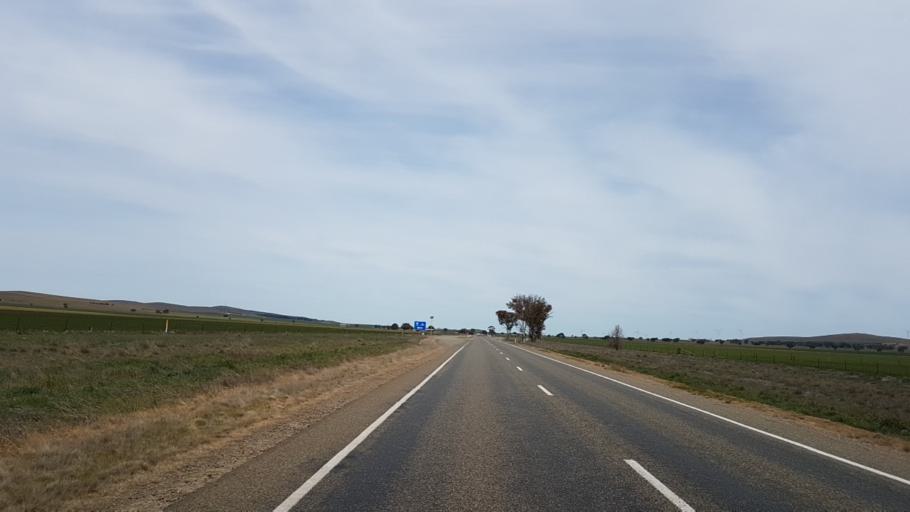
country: AU
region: South Australia
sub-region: Northern Areas
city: Jamestown
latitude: -33.0542
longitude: 138.6178
